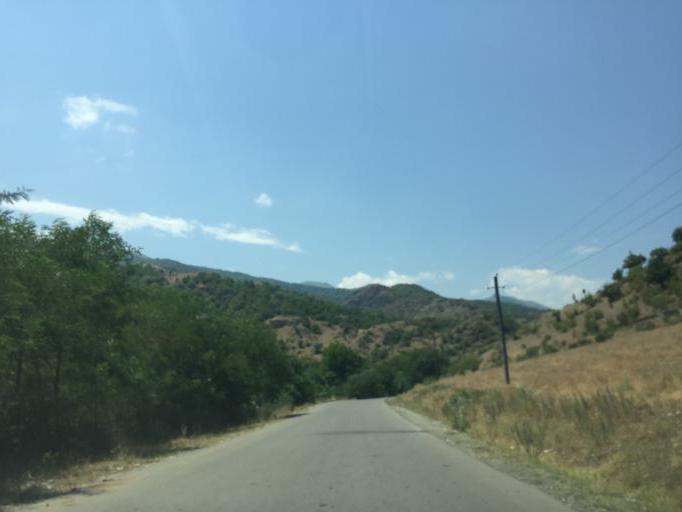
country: AZ
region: Kalbacar Rayonu
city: Kerbakhiar
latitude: 40.1365
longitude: 46.3547
